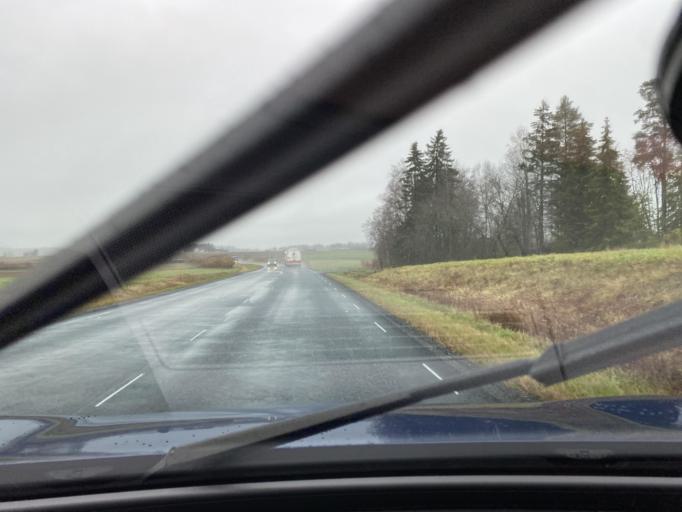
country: FI
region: Haeme
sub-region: Forssa
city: Ypaejae
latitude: 60.7820
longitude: 23.3071
